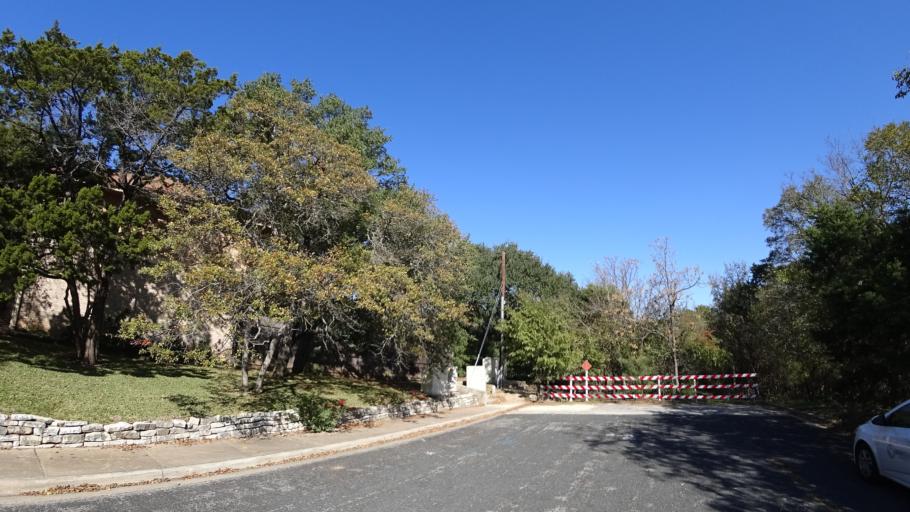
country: US
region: Texas
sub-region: Williamson County
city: Jollyville
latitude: 30.4157
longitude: -97.7588
